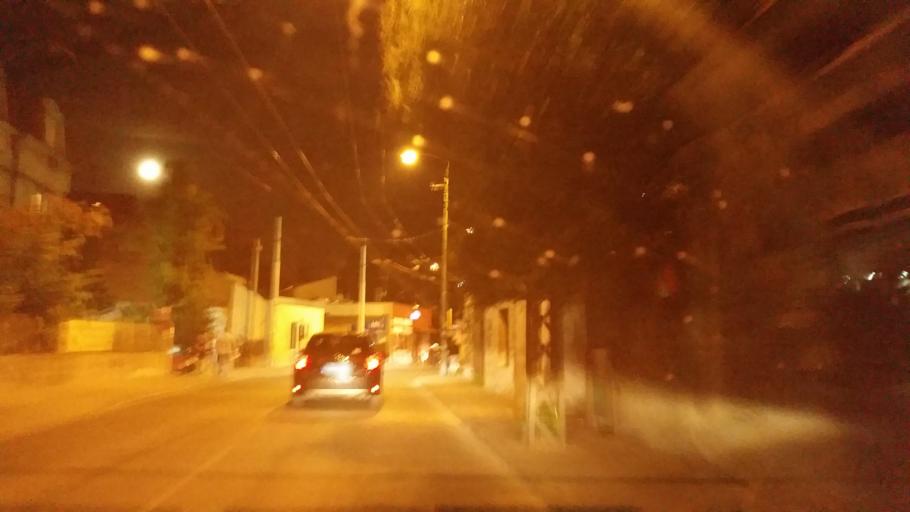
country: RS
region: Central Serbia
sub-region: Belgrade
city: Vracar
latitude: 44.7966
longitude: 20.4890
